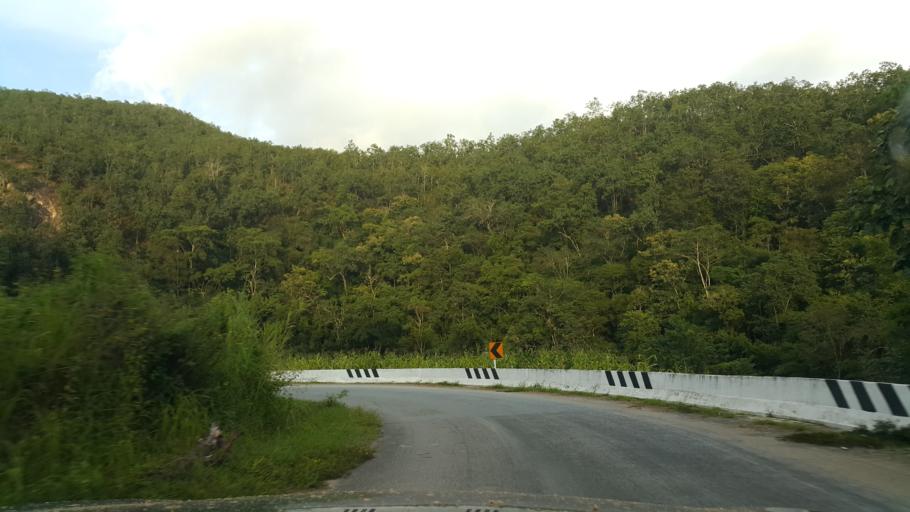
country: TH
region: Mae Hong Son
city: Mae Hi
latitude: 19.2028
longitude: 98.4314
